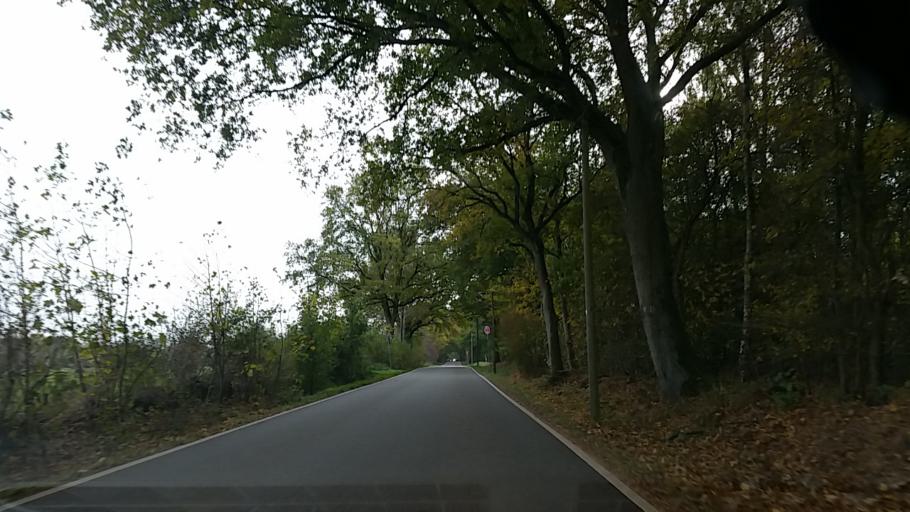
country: DE
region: Schleswig-Holstein
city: Barsbuettel
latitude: 53.5596
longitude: 10.1496
